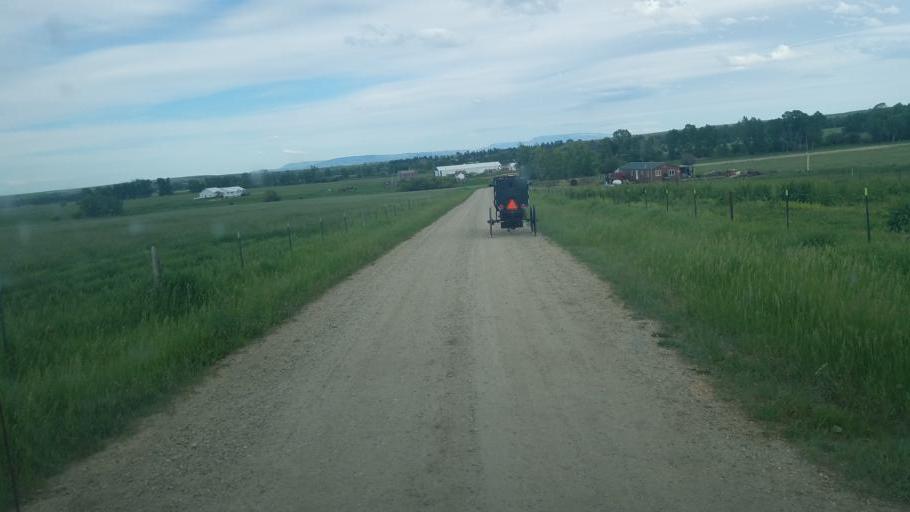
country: US
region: Montana
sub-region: Carbon County
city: Red Lodge
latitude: 45.3635
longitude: -109.1908
